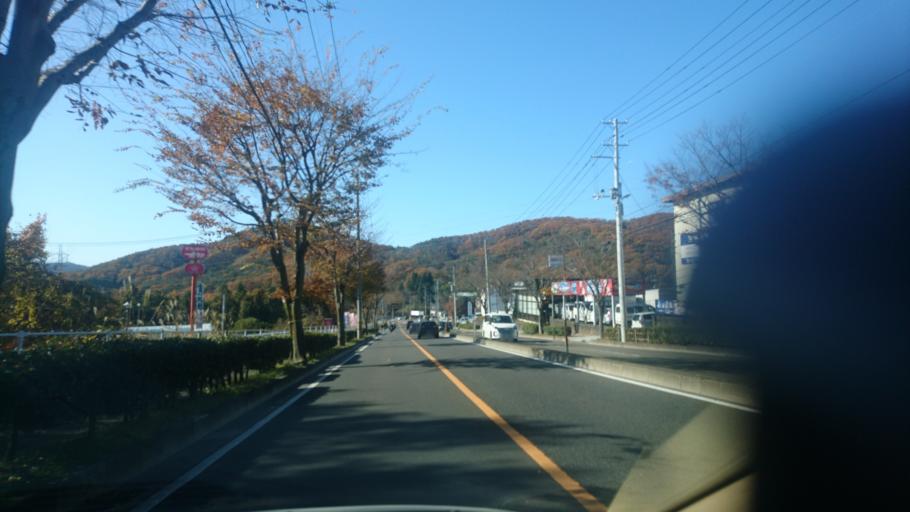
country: JP
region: Miyagi
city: Sendai
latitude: 38.2835
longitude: 140.8144
